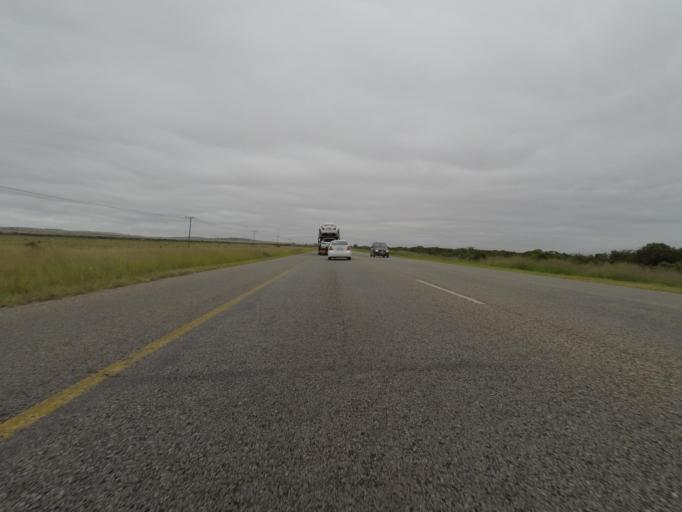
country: ZA
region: Eastern Cape
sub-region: Nelson Mandela Bay Metropolitan Municipality
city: Port Elizabeth
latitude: -33.6577
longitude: 25.8632
